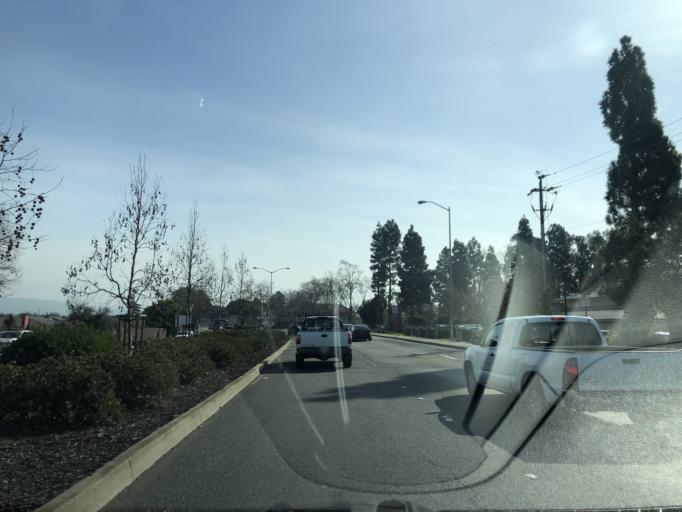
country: US
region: California
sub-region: Alameda County
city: Union City
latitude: 37.5975
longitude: -122.0579
